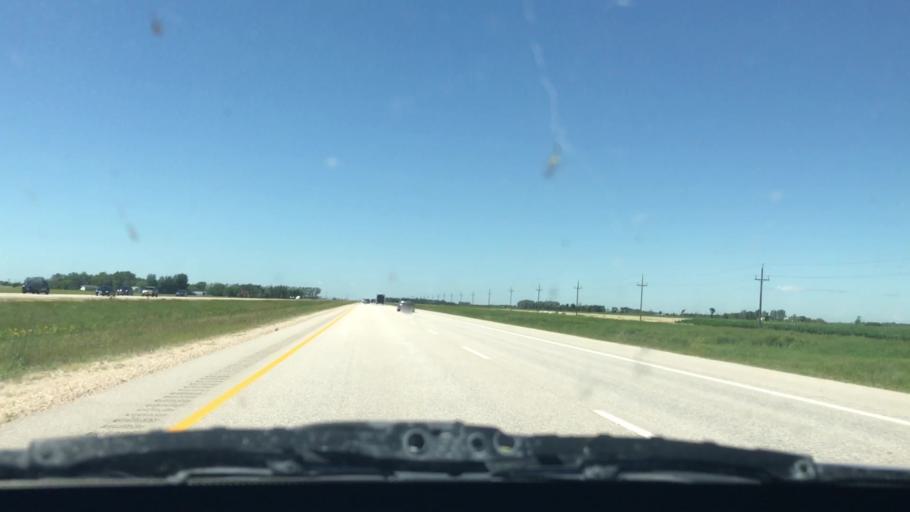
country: CA
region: Manitoba
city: Steinbach
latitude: 49.7279
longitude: -96.7128
